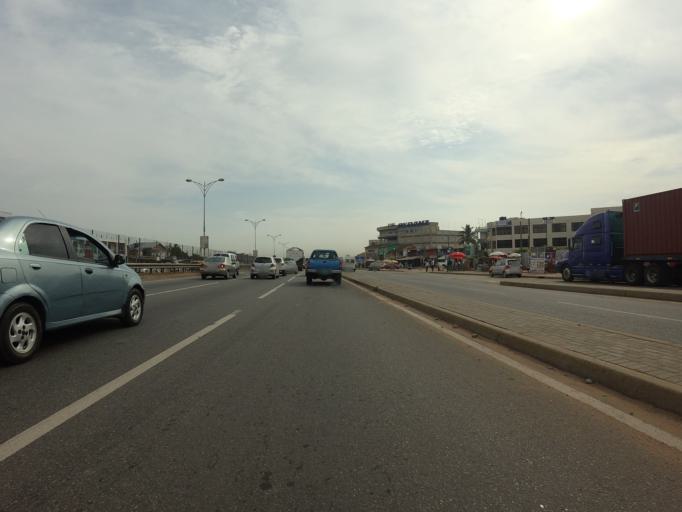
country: GH
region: Greater Accra
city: Dome
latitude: 5.6052
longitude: -0.2512
